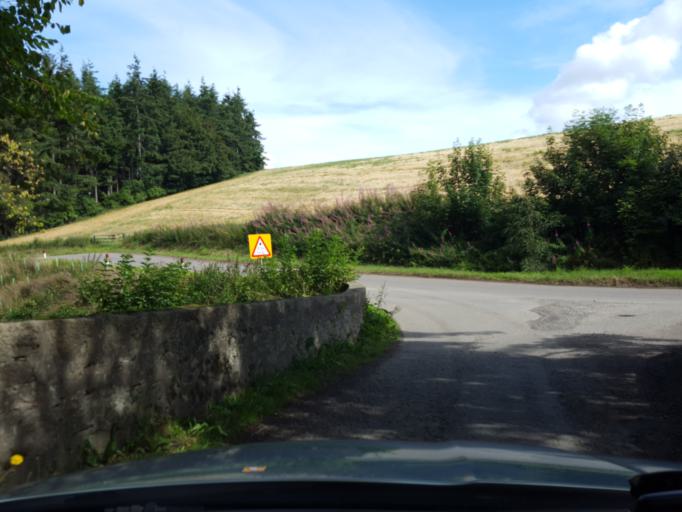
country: GB
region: Scotland
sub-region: Moray
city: Rothes
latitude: 57.4762
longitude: -3.1967
